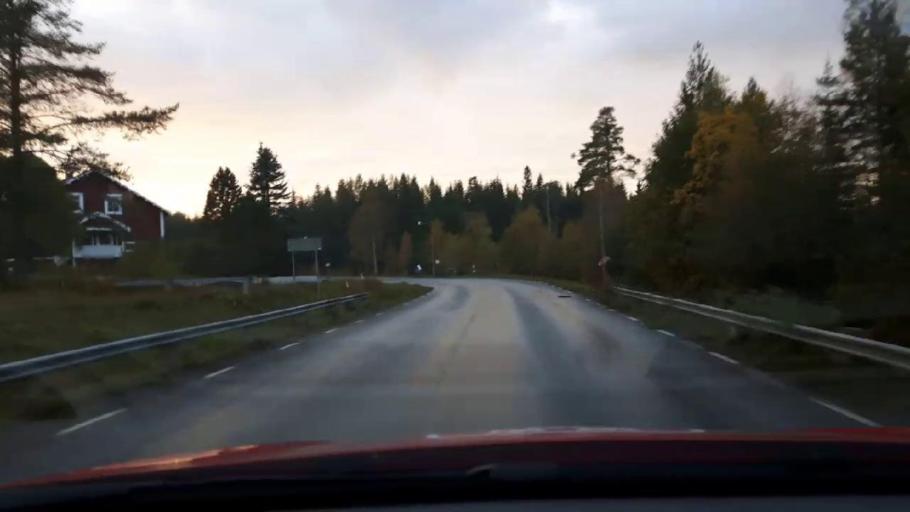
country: SE
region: Jaemtland
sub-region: OEstersunds Kommun
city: Lit
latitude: 63.3263
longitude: 14.8730
